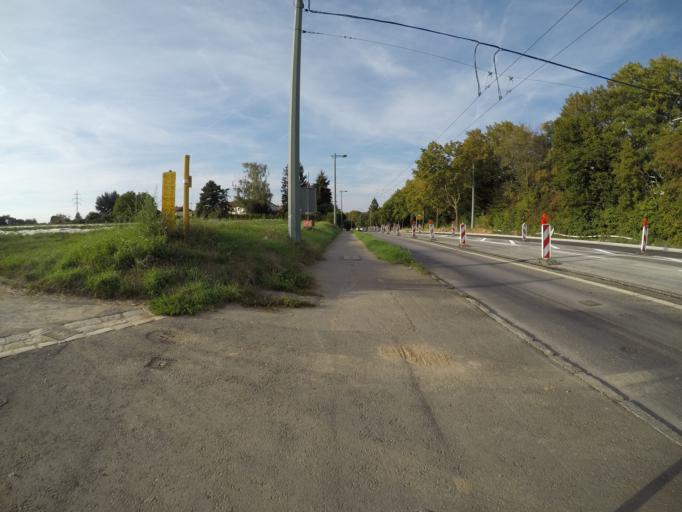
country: DE
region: Baden-Wuerttemberg
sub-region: Regierungsbezirk Stuttgart
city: Esslingen
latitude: 48.7231
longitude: 9.3023
